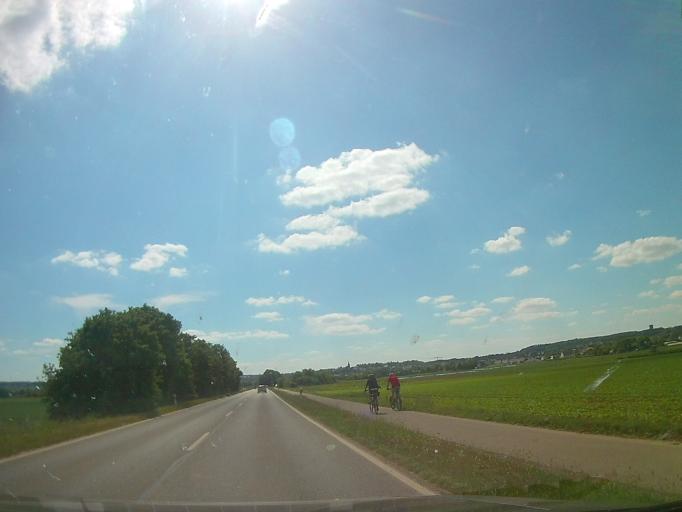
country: DE
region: North Rhine-Westphalia
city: Bruhl
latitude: 50.8187
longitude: 6.9164
